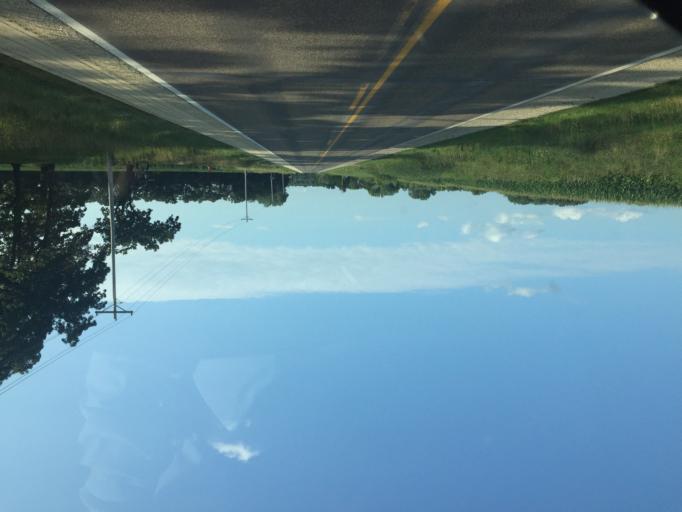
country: US
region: Minnesota
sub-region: Olmsted County
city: Rochester
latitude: 43.9669
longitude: -92.5581
